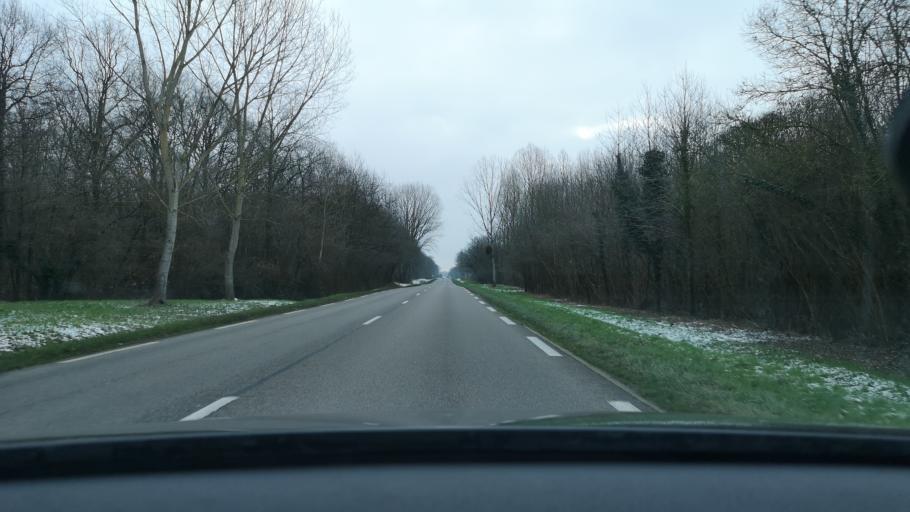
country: FR
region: Bourgogne
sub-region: Departement de Saone-et-Loire
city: Epervans
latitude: 46.7784
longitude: 4.9490
